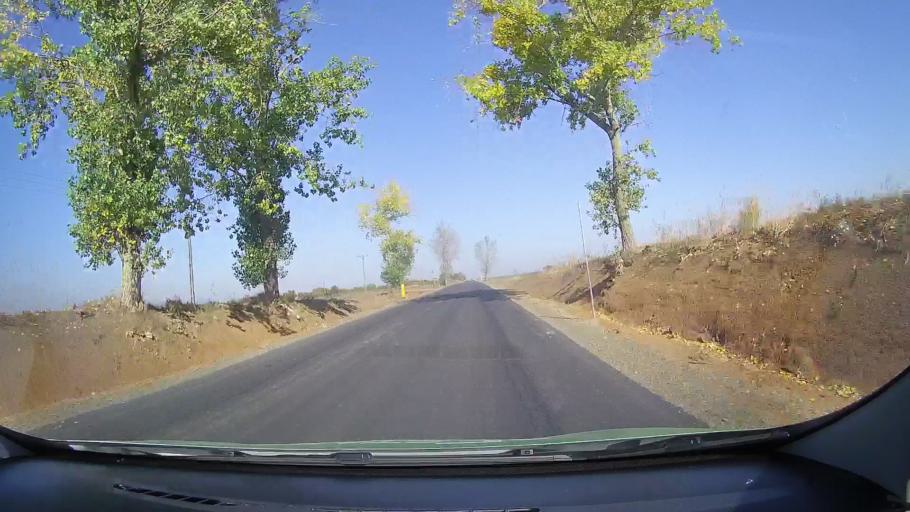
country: RO
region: Satu Mare
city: Carei
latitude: 47.6542
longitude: 22.4613
